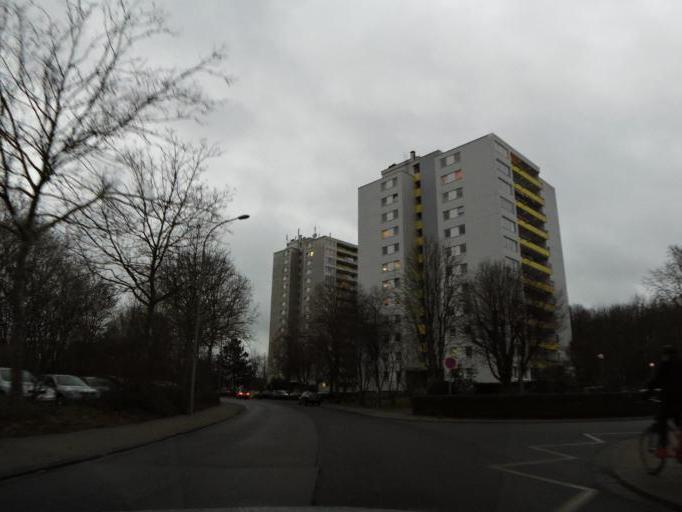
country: DE
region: Hesse
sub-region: Regierungsbezirk Darmstadt
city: Gross-Gerau
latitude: 49.9100
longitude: 8.4835
